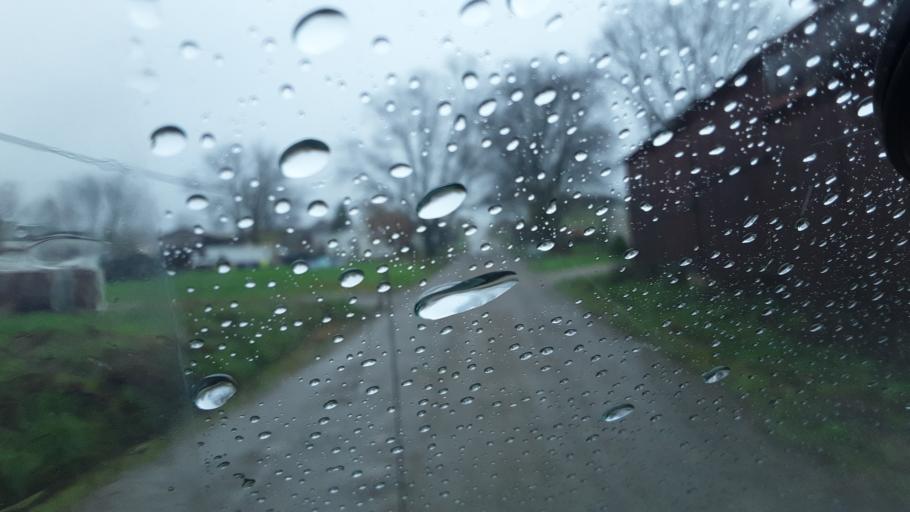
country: US
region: Ohio
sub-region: Vinton County
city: McArthur
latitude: 39.2256
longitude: -82.4725
